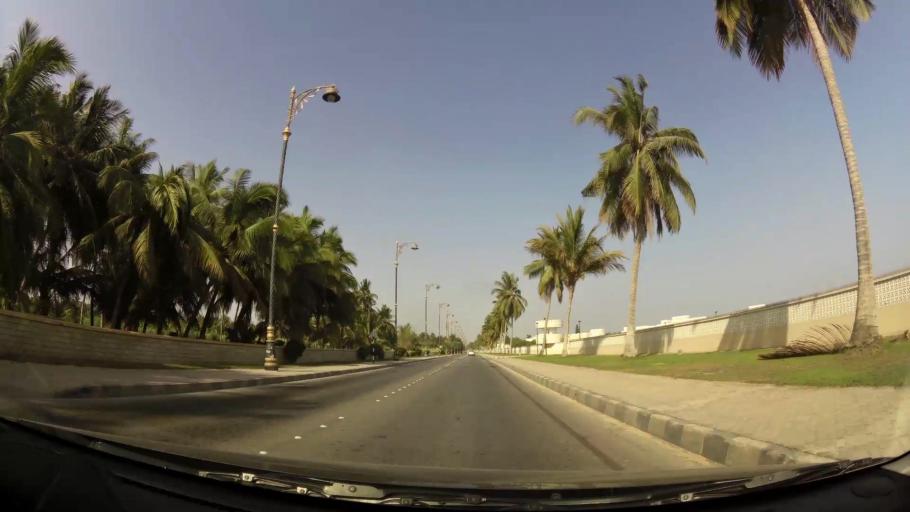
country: OM
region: Zufar
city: Salalah
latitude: 16.9994
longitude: 54.0822
